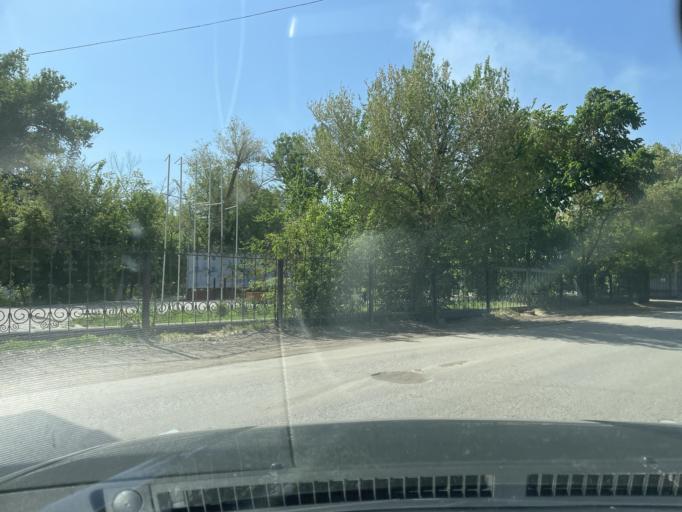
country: KZ
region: Qaraghandy
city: Zhezqazghan
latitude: 47.7898
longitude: 67.7151
